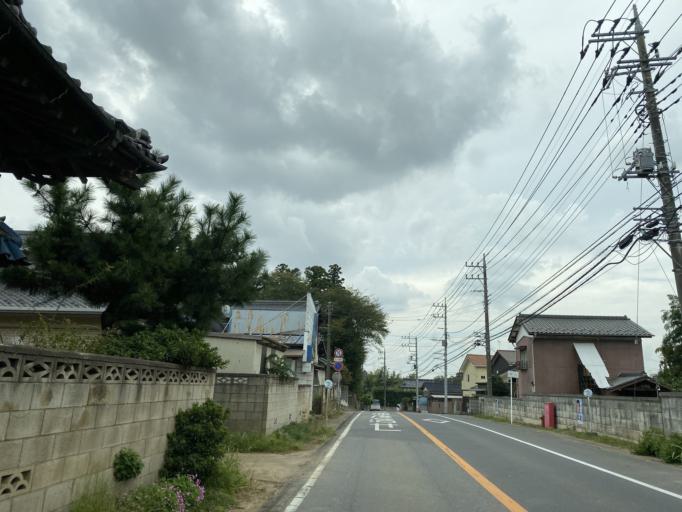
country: JP
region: Ibaraki
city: Mitsukaido
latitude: 35.9882
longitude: 140.0437
